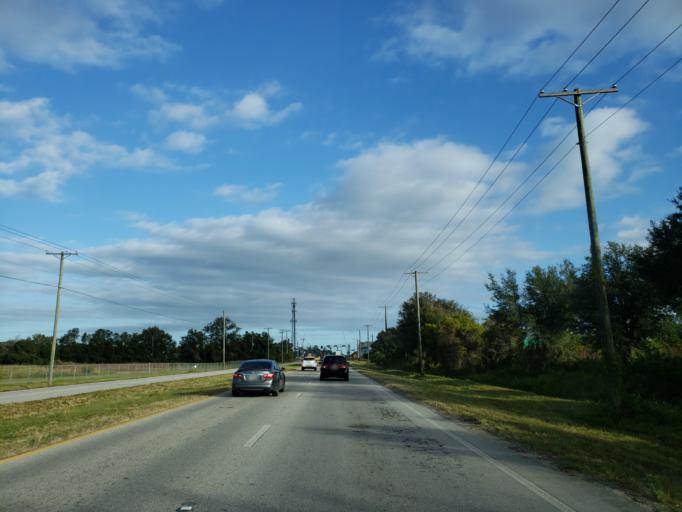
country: US
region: Florida
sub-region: Hillsborough County
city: Plant City
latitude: 28.0161
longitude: -82.1049
